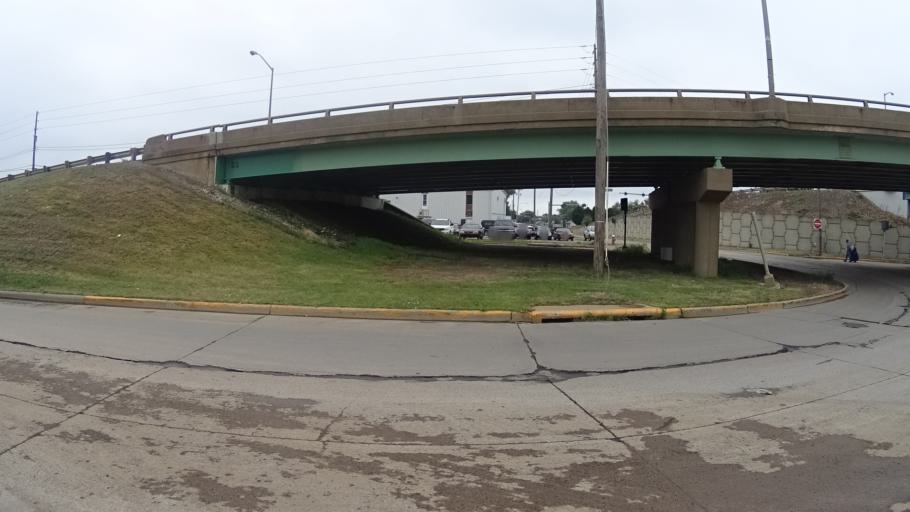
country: US
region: Ohio
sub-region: Erie County
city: Sandusky
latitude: 41.4389
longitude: -82.6948
